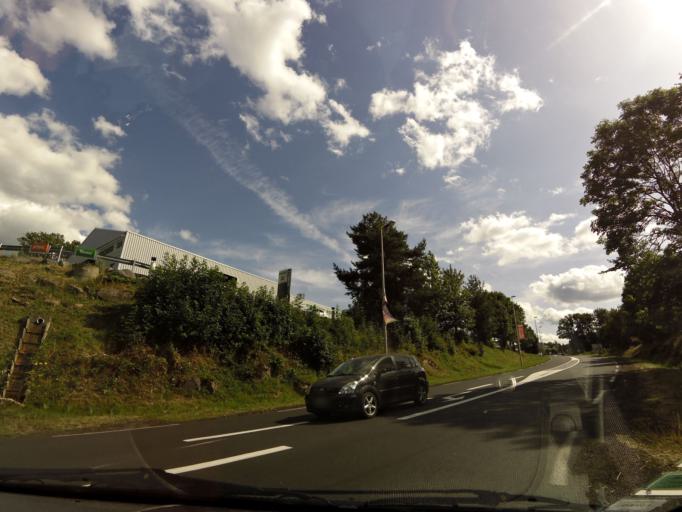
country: FR
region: Auvergne
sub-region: Departement du Puy-de-Dome
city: Mont-Dore
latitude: 45.5148
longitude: 2.9399
